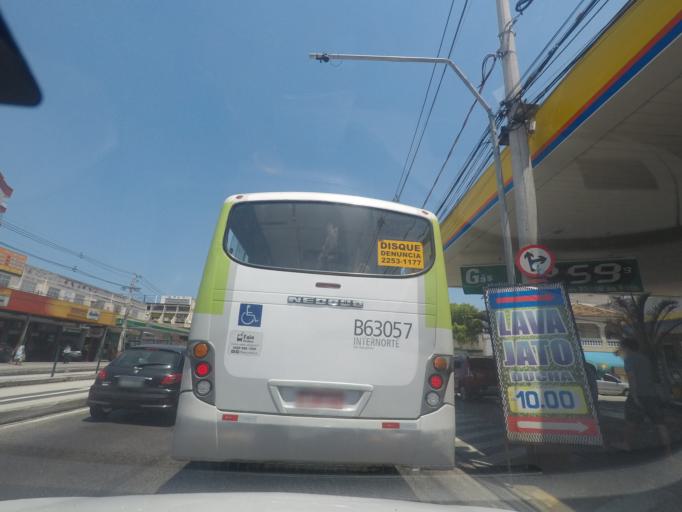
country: BR
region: Rio de Janeiro
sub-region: Duque De Caxias
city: Duque de Caxias
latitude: -22.8403
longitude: -43.2815
